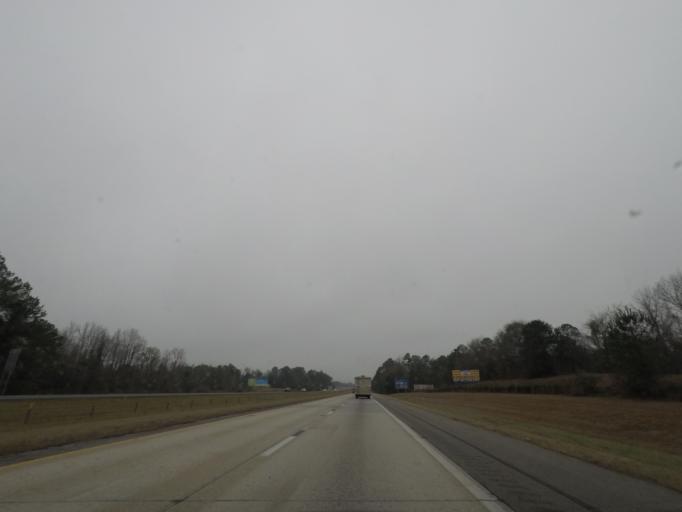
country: US
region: South Carolina
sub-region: Clarendon County
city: Manning
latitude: 33.7138
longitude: -80.2356
